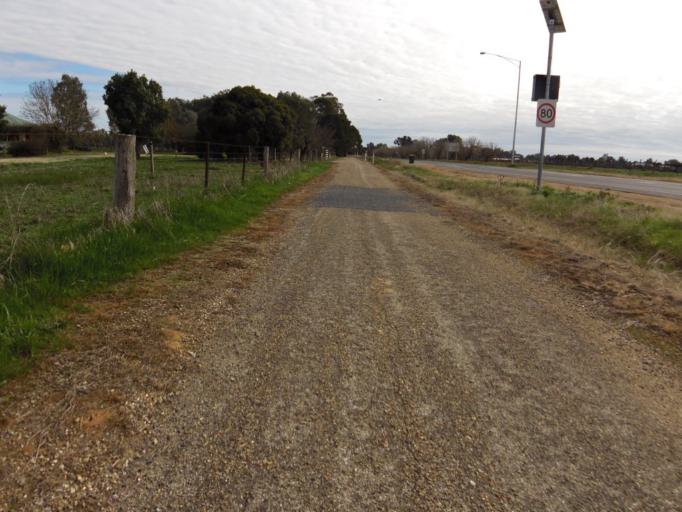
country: AU
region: Victoria
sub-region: Wangaratta
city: Wangaratta
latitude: -36.4393
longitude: 146.3601
